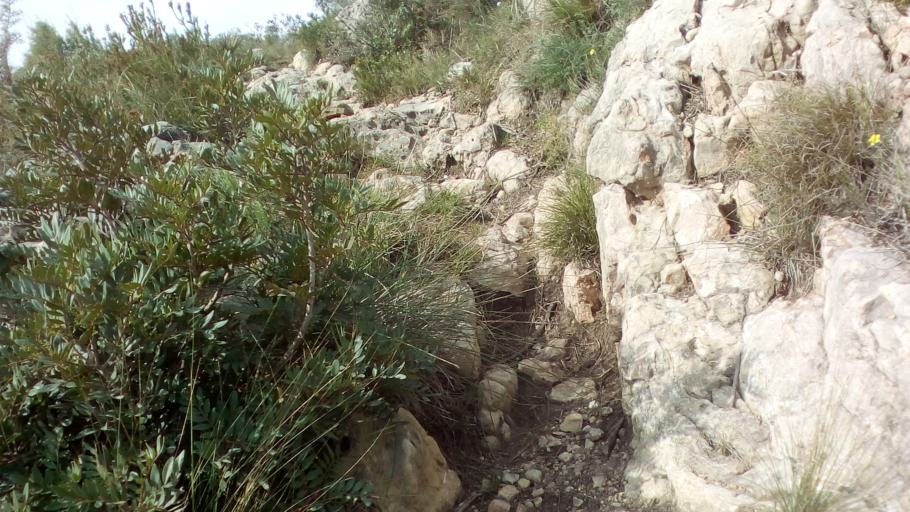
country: ES
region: Valencia
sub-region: Provincia de Valencia
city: Xeraco,Jaraco
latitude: 39.0390
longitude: -0.2431
